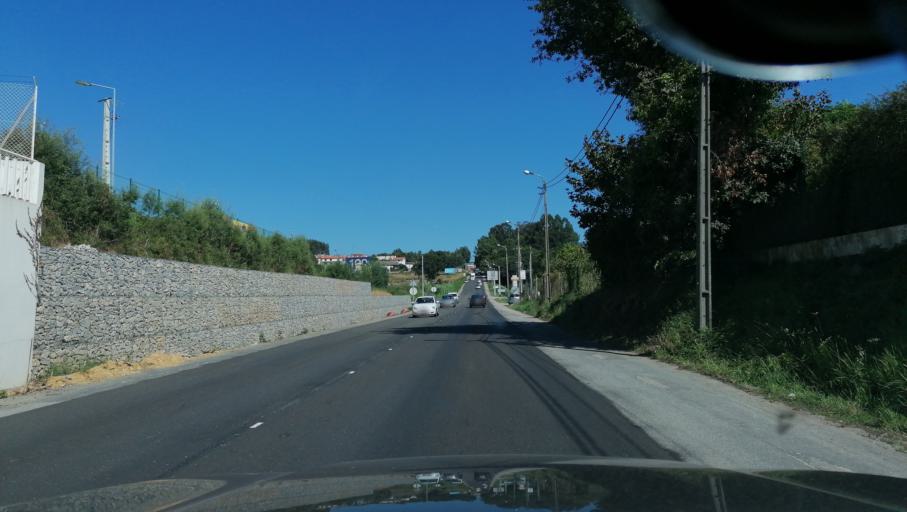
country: PT
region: Aveiro
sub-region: Santa Maria da Feira
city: Feira
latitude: 40.9312
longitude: -8.5251
